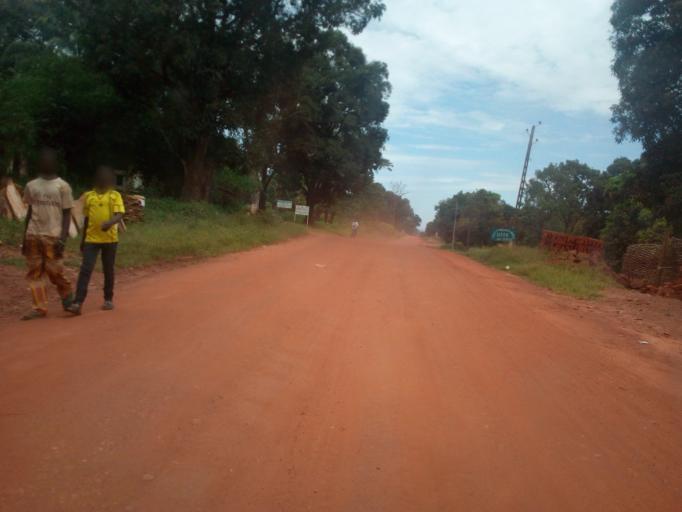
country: CF
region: Ouaka
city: Bambari
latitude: 5.7696
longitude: 20.6721
